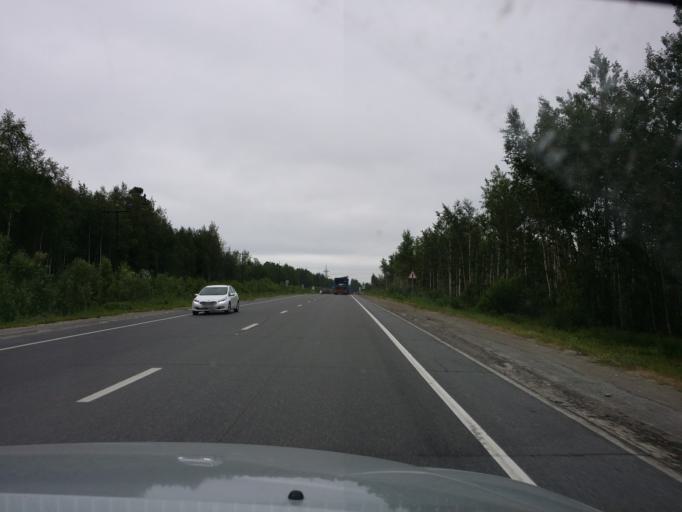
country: RU
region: Khanty-Mansiyskiy Avtonomnyy Okrug
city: Nizhnevartovsk
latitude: 61.0209
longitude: 76.3782
